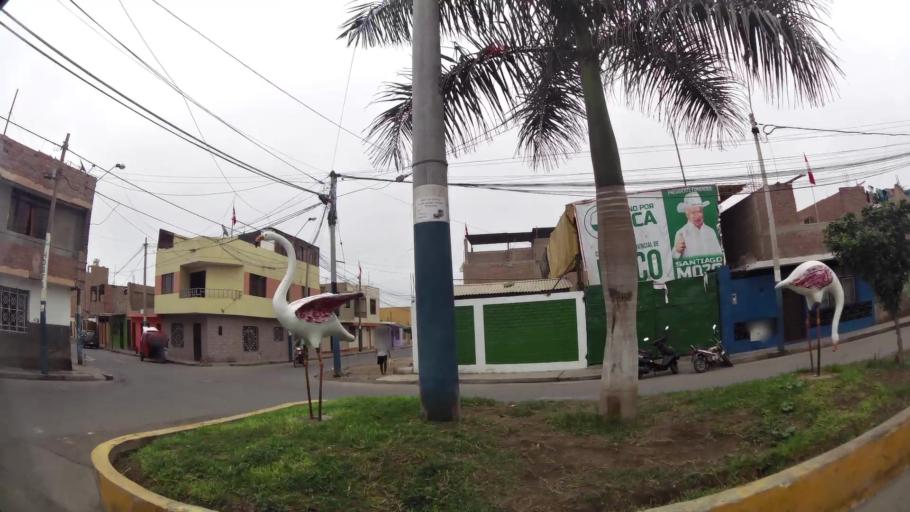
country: PE
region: Ica
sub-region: Provincia de Pisco
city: Pisco
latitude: -13.7085
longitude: -76.2000
